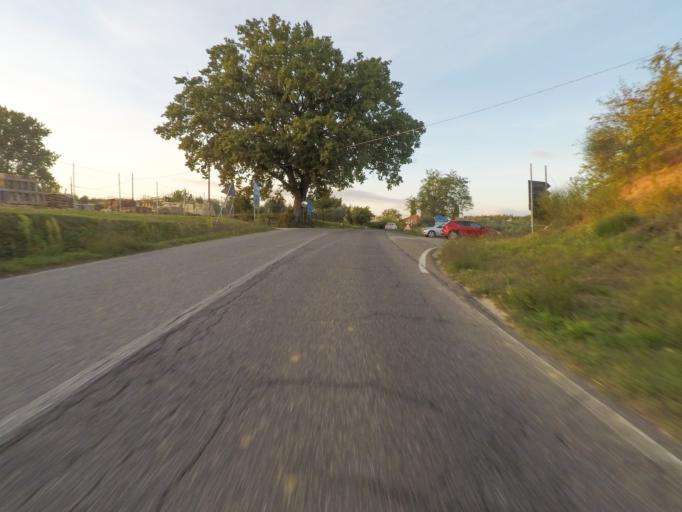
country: IT
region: Tuscany
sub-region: Provincia di Siena
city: Montepulciano
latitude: 43.1293
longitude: 11.7280
